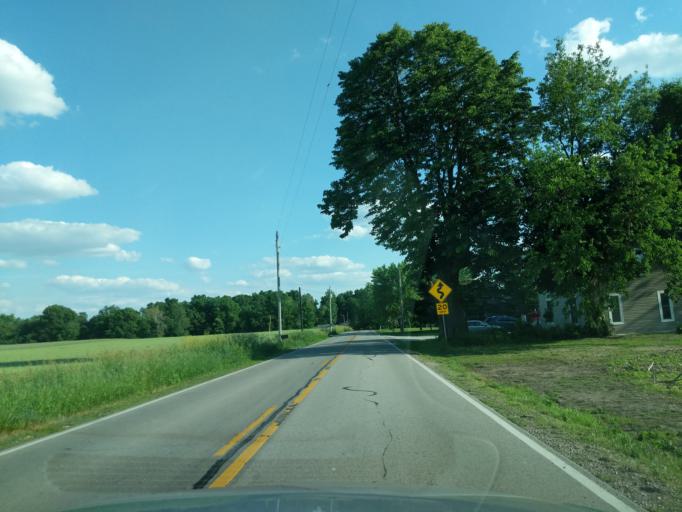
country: US
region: Indiana
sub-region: Kosciusko County
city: North Webster
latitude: 41.3123
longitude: -85.6406
